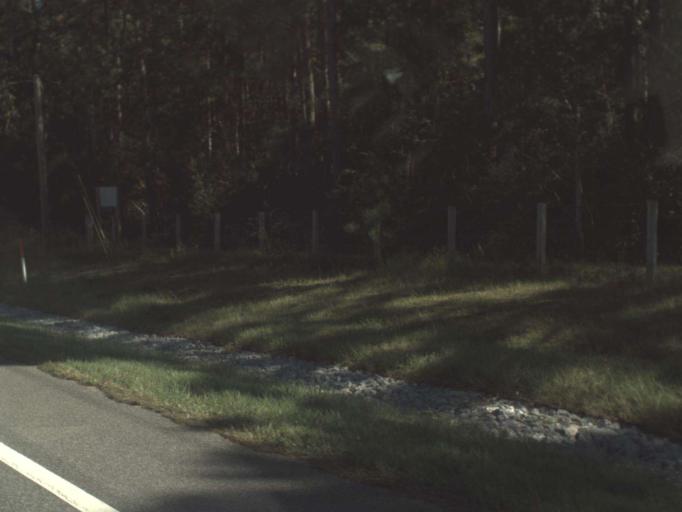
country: US
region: Florida
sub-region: Walton County
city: Freeport
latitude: 30.4786
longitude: -86.0671
